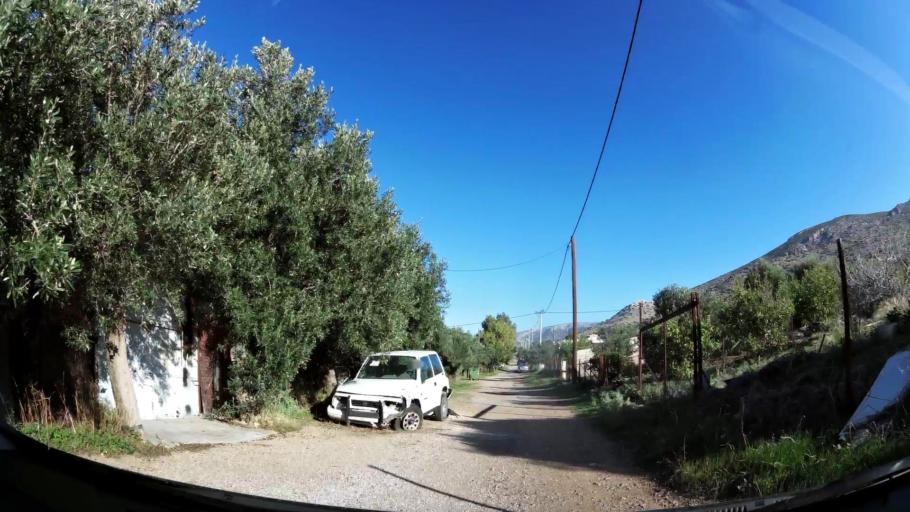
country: GR
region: Attica
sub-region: Nomarchia Athinas
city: Glyfada
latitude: 37.8703
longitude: 23.7742
